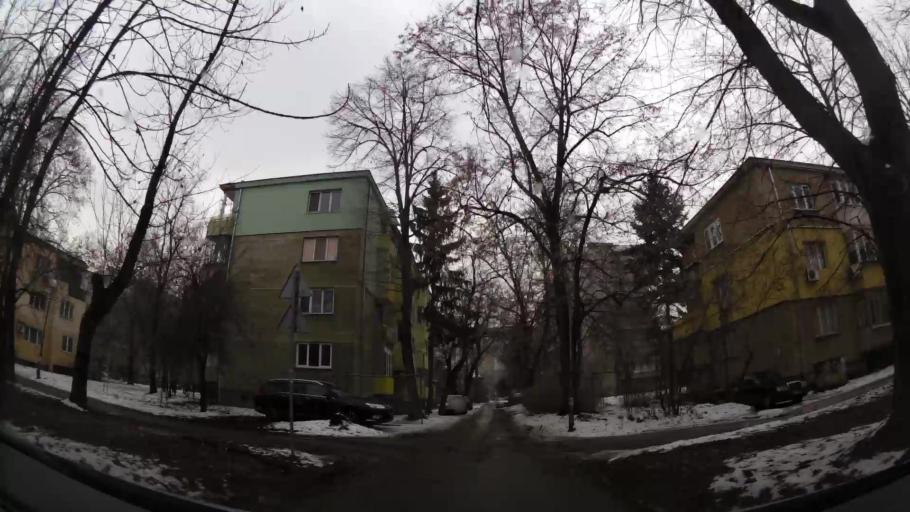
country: BG
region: Sofia-Capital
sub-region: Stolichna Obshtina
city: Sofia
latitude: 42.6810
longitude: 23.2935
